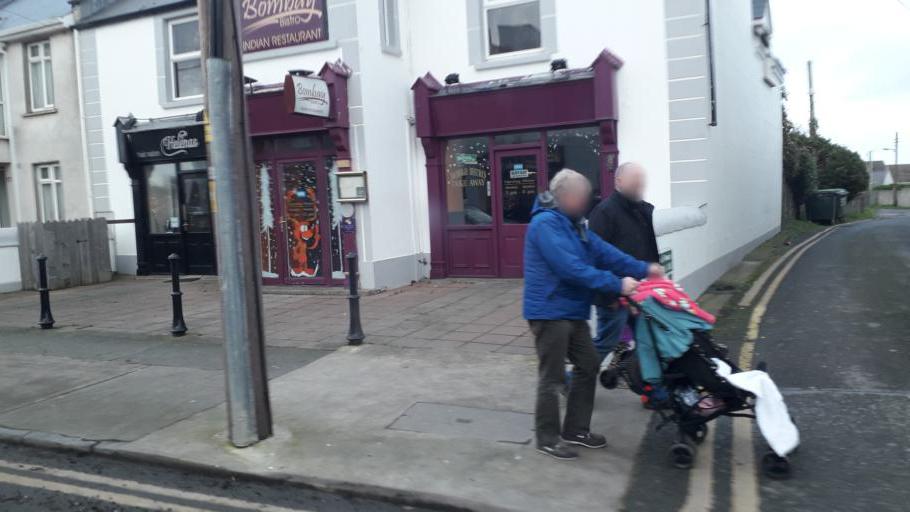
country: IE
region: Leinster
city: An Ros
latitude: 53.5225
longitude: -6.0956
